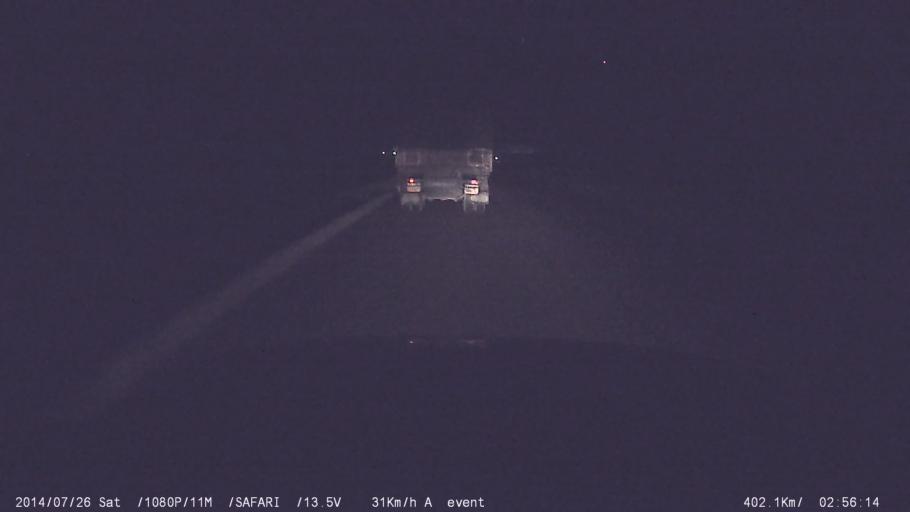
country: IN
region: Kerala
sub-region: Palakkad district
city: Palakkad
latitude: 10.7387
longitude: 76.6387
